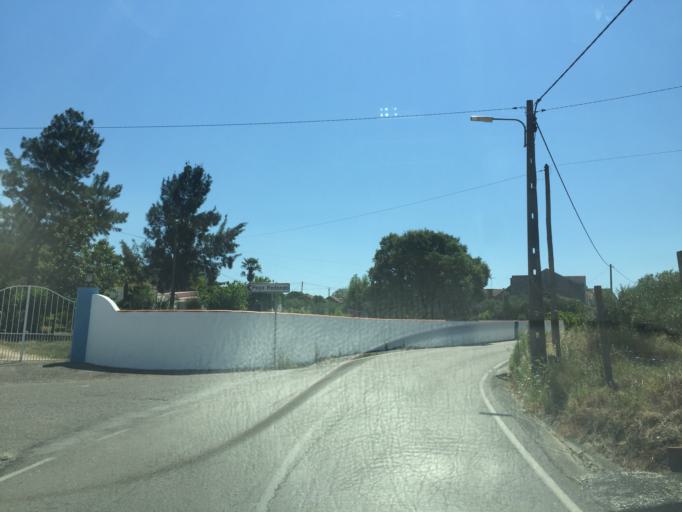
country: PT
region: Santarem
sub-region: Ferreira do Zezere
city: Ferreira do Zezere
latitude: 39.6222
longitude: -8.3158
